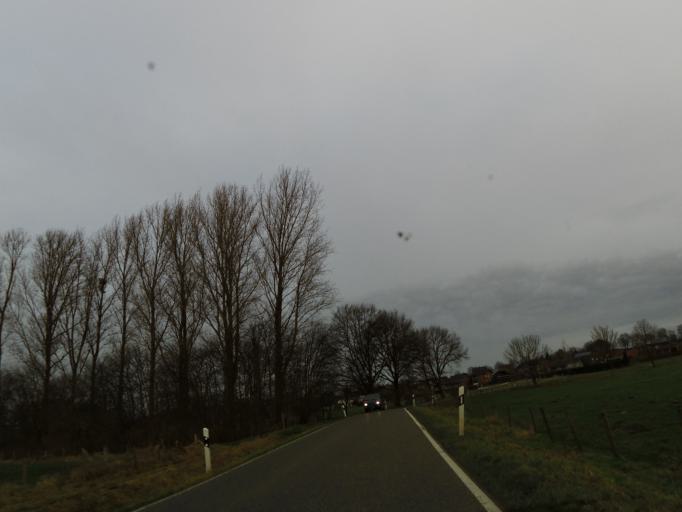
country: DE
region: North Rhine-Westphalia
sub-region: Regierungsbezirk Koln
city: Gangelt
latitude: 50.9852
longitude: 6.0255
